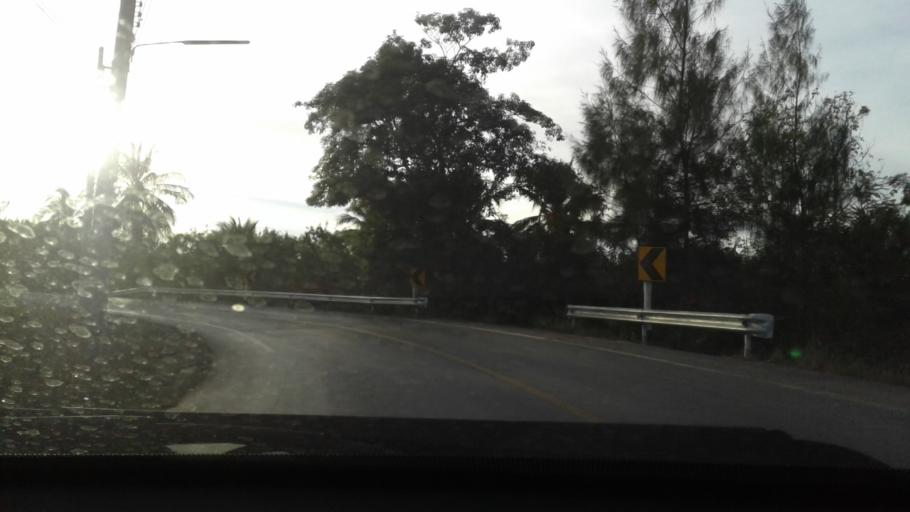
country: TH
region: Nonthaburi
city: Sai Noi
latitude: 13.9036
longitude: 100.2505
